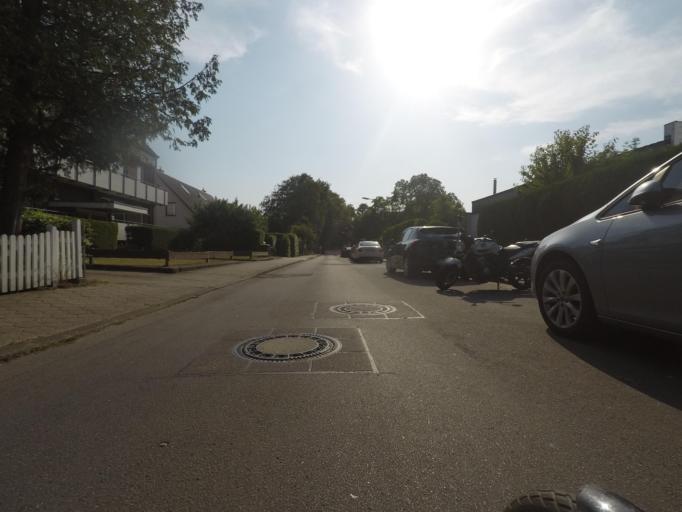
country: DE
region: Hamburg
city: Farmsen-Berne
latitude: 53.6203
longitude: 10.1385
